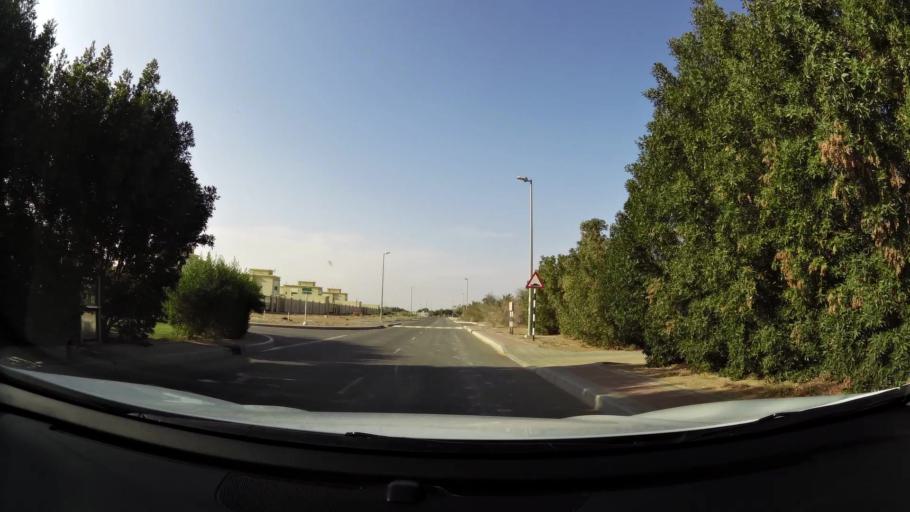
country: AE
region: Abu Dhabi
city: Al Ain
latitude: 24.0622
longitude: 55.8431
